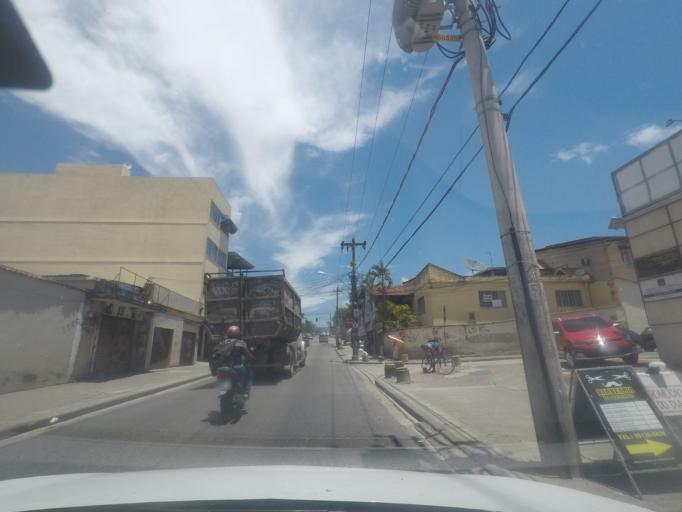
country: BR
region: Rio de Janeiro
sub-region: Itaguai
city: Itaguai
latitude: -22.9149
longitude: -43.6865
